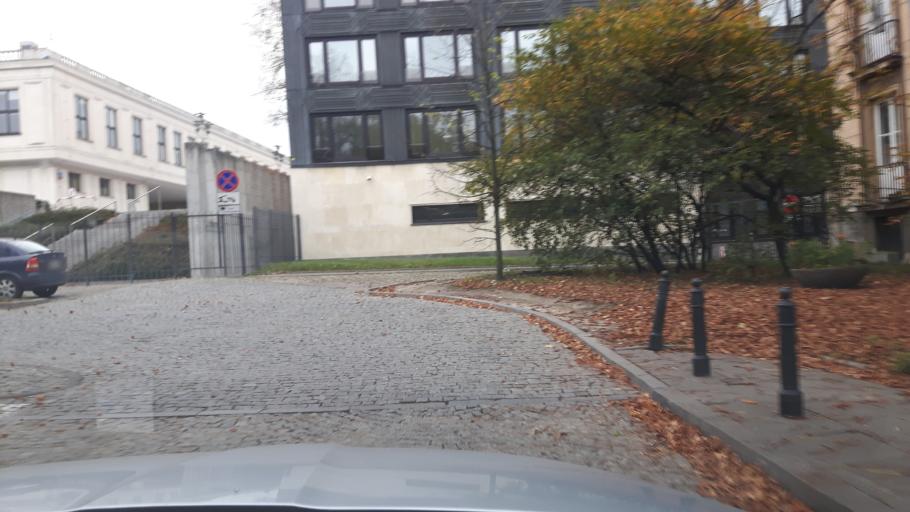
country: PL
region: Masovian Voivodeship
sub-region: Warszawa
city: Srodmiescie
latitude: 52.2271
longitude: 21.0287
